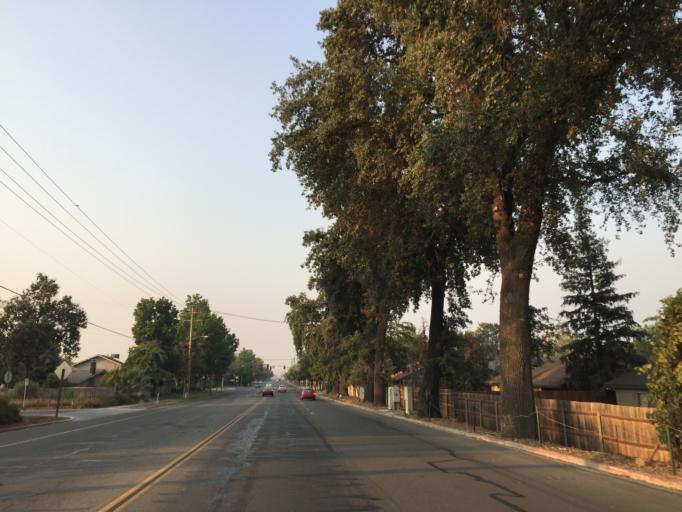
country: US
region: California
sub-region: Tulare County
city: Visalia
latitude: 36.3521
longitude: -119.2789
